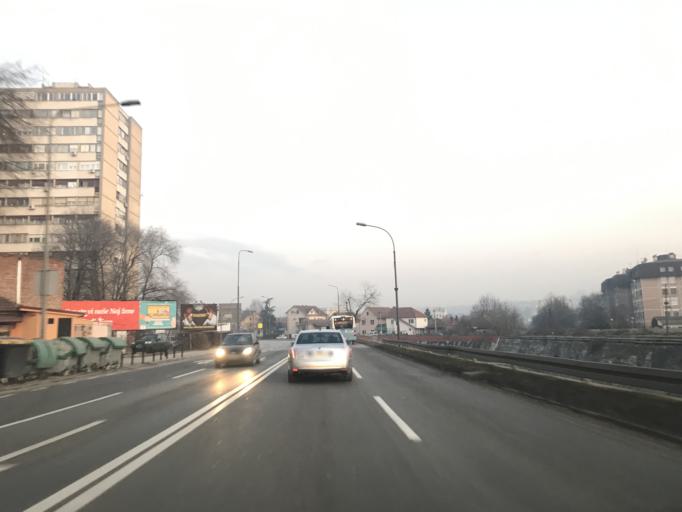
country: RS
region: Central Serbia
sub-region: Sumadijski Okrug
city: Kragujevac
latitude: 44.0089
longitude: 20.9150
